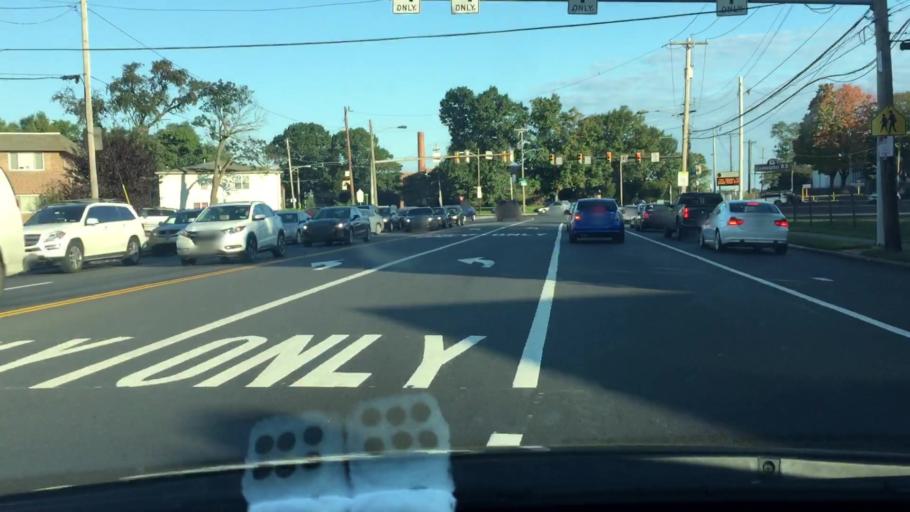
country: US
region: New Jersey
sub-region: Burlington County
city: Riverton
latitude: 40.0528
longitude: -75.0083
